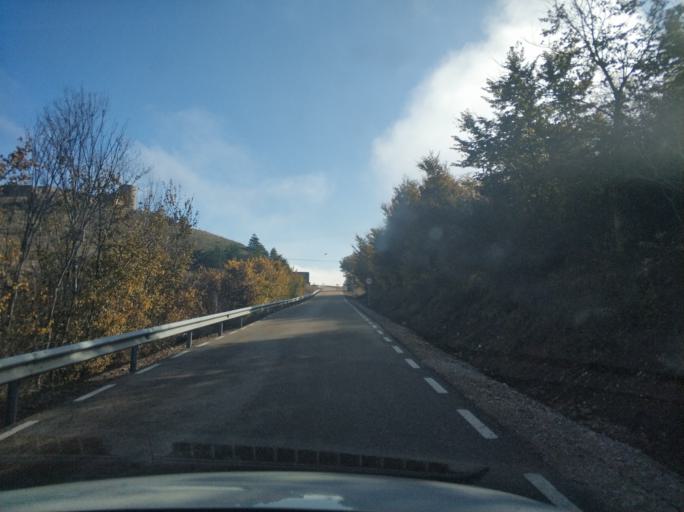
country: ES
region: Castille and Leon
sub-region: Provincia de Soria
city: Medinaceli
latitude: 41.1695
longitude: -2.4401
